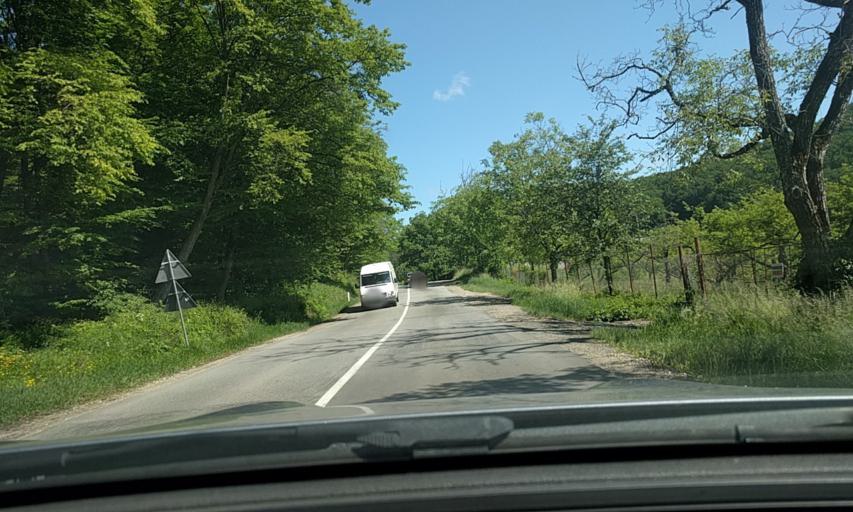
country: RO
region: Bistrita-Nasaud
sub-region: Comuna Dumitra
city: Dumitra
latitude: 47.1851
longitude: 24.4842
